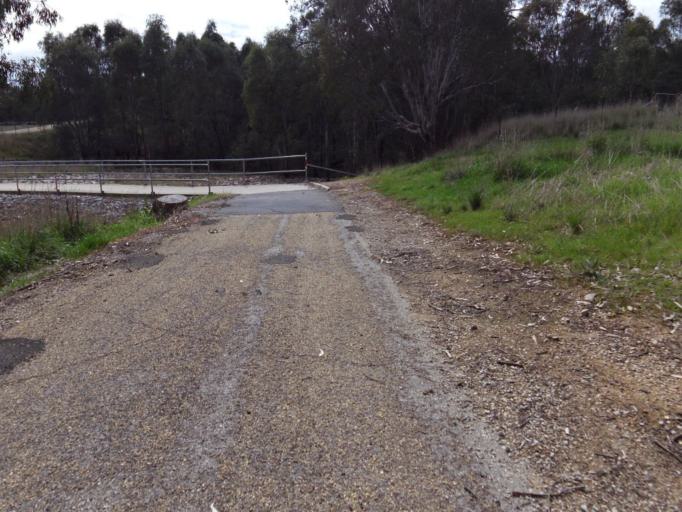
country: AU
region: Victoria
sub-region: Wangaratta
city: Wangaratta
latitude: -36.3937
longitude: 146.3435
